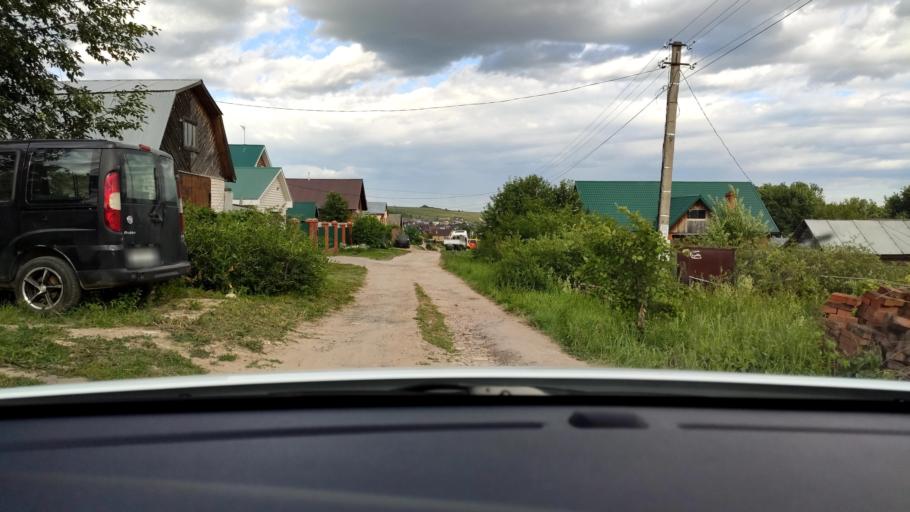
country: RU
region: Tatarstan
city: Stolbishchi
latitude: 55.7534
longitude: 49.2873
